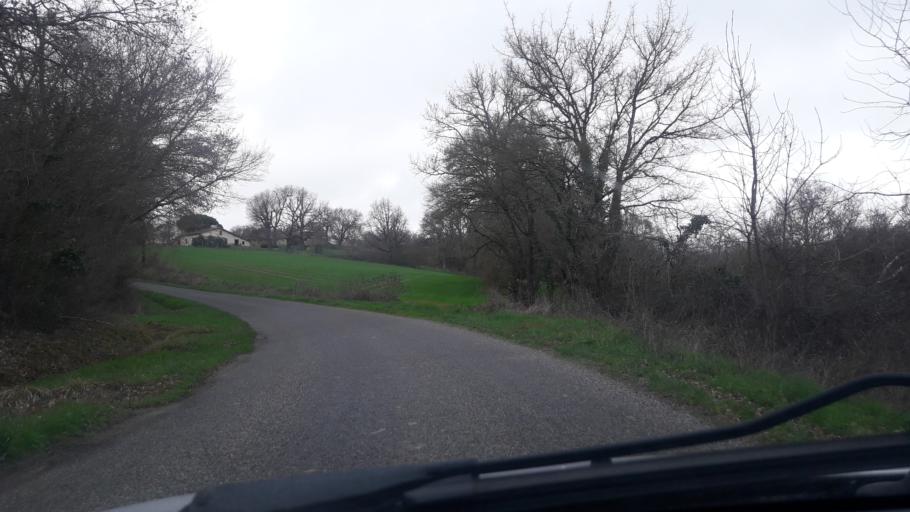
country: FR
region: Midi-Pyrenees
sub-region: Departement du Gers
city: Gimont
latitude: 43.6567
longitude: 0.9752
